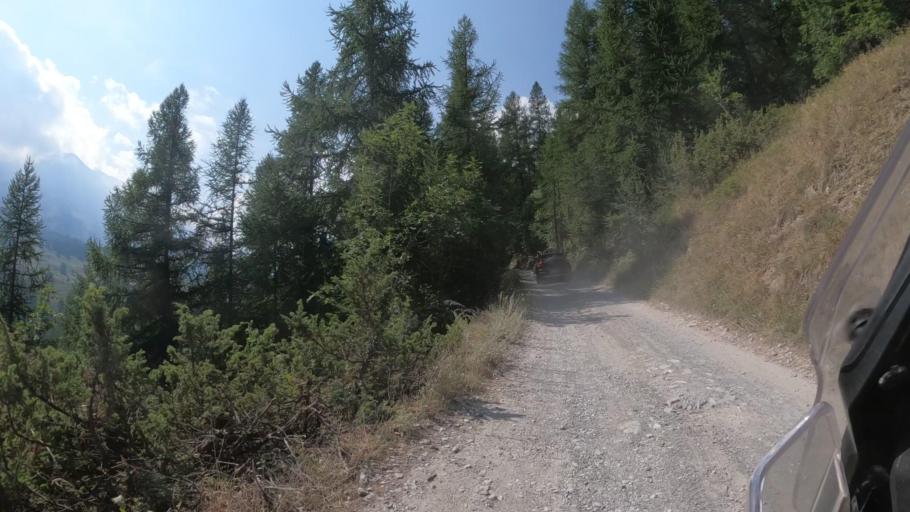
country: IT
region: Piedmont
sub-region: Provincia di Torino
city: Cesana Torinese
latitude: 44.9288
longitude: 6.8134
